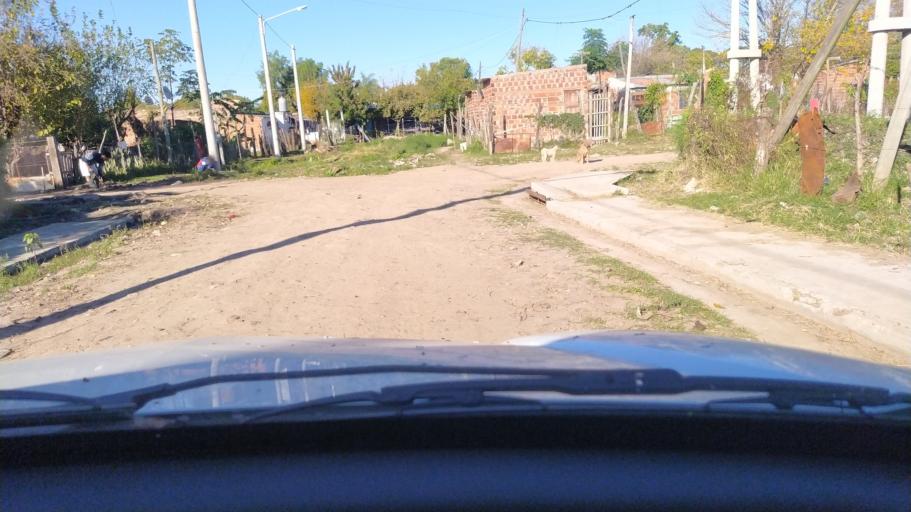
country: AR
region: Corrientes
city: Corrientes
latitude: -27.4980
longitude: -58.8097
